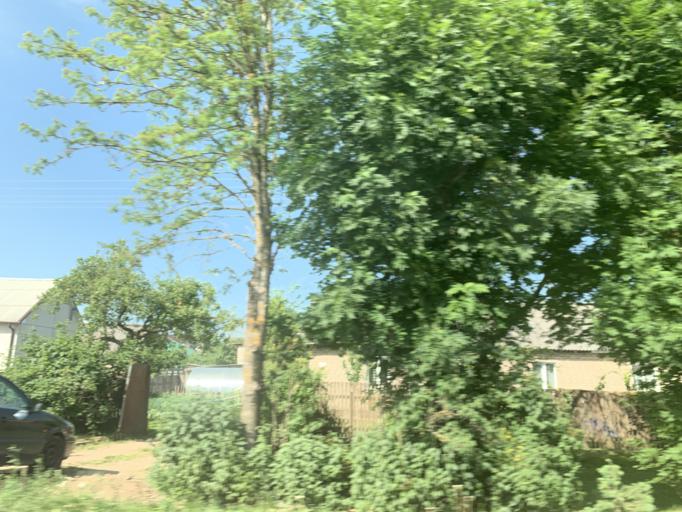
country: BY
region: Minsk
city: Dzyarzhynsk
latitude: 53.6988
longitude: 27.1022
